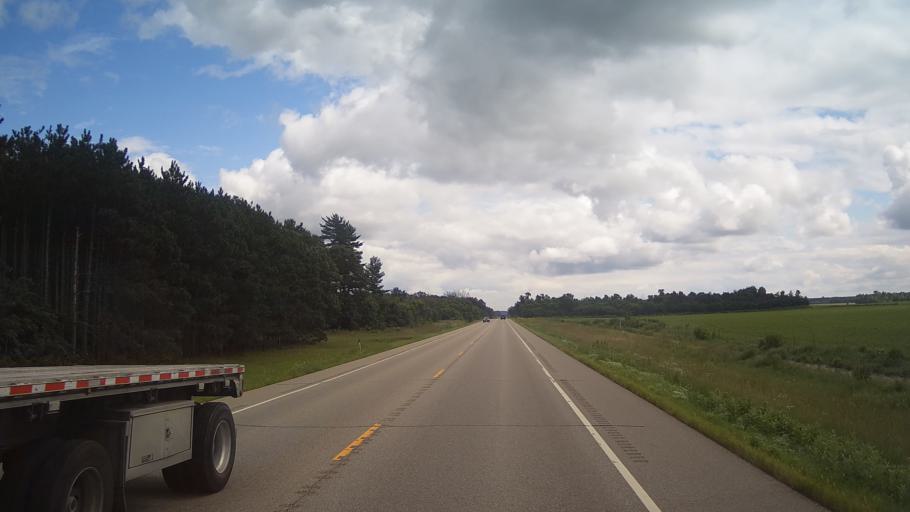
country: US
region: Wisconsin
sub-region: Adams County
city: Friendship
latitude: 44.0219
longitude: -89.6549
